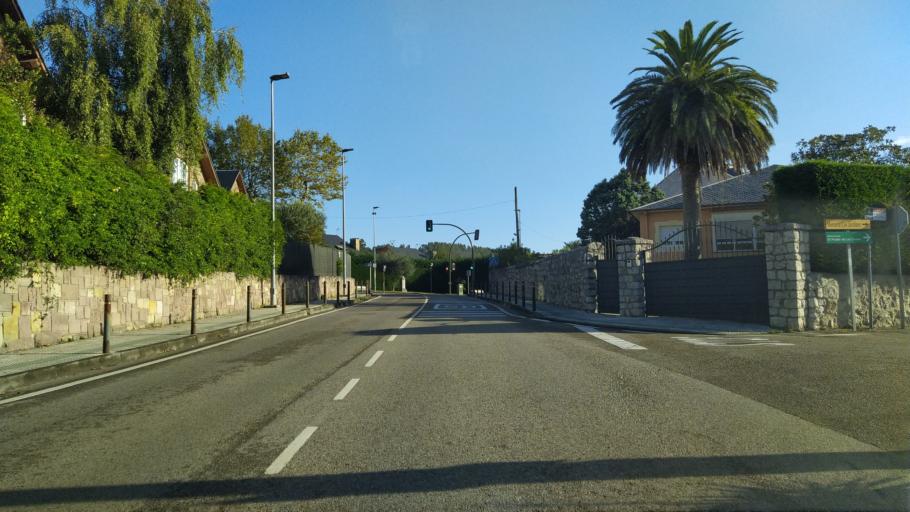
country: ES
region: Cantabria
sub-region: Provincia de Cantabria
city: Santa Cruz de Bezana
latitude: 43.4437
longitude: -3.9296
